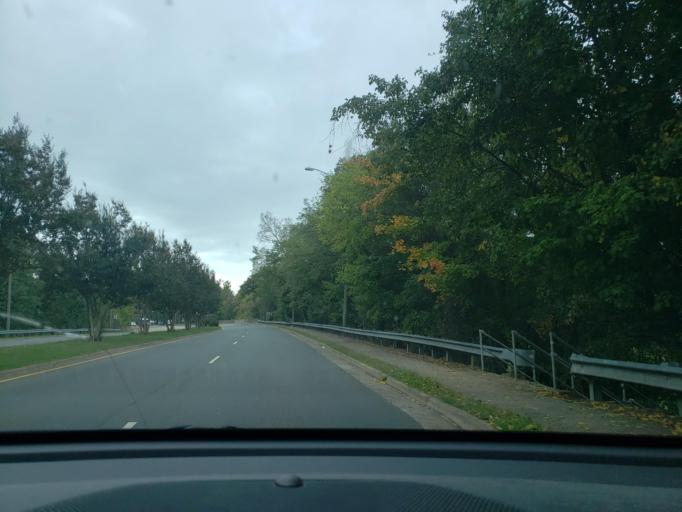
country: US
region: Virginia
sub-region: City of Fredericksburg
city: Fredericksburg
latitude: 38.2935
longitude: -77.4569
